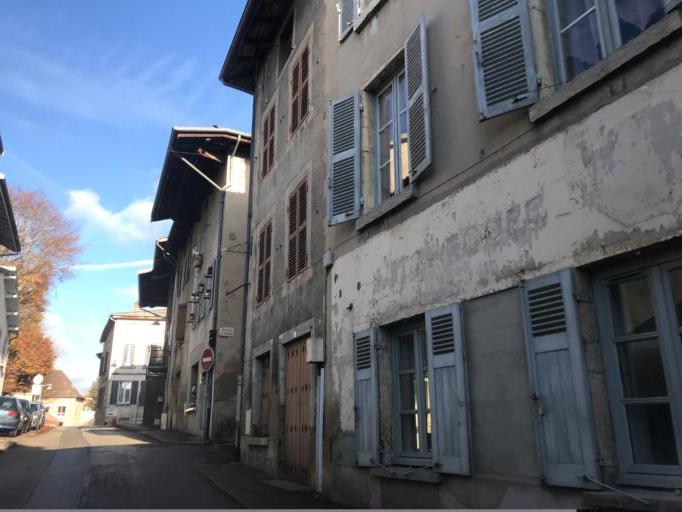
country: FR
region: Rhone-Alpes
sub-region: Departement de l'Ain
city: Jujurieux
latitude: 46.0405
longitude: 5.4095
